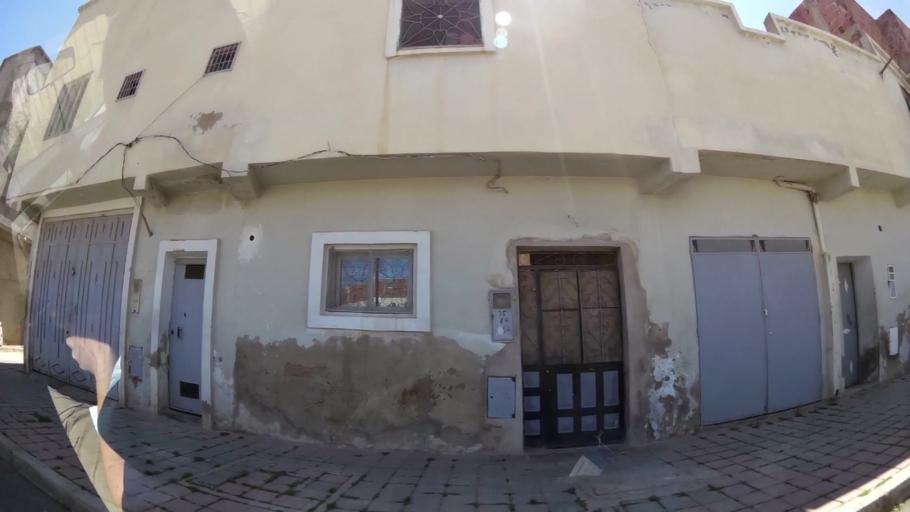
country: MA
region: Oriental
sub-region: Oujda-Angad
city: Oujda
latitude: 34.6942
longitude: -1.9454
